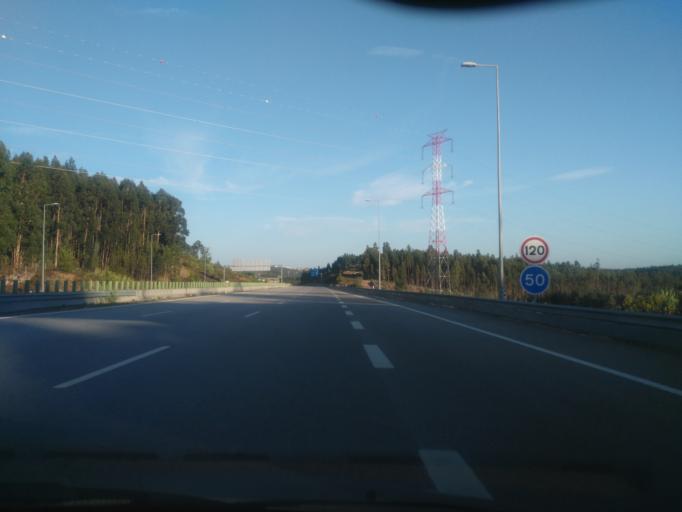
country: PT
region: Coimbra
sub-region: Figueira da Foz
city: Alhadas
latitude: 40.1563
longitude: -8.7731
